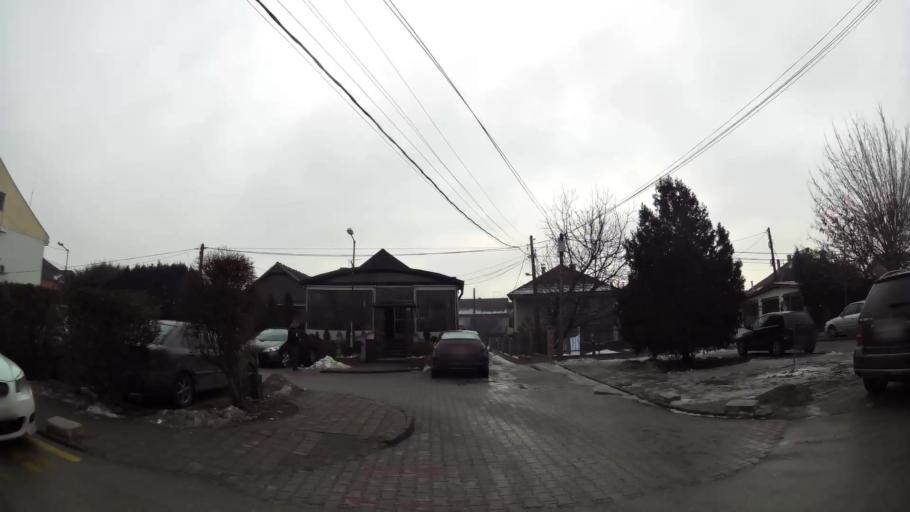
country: MK
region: Ilinden
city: Ilinden
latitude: 41.9945
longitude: 21.5751
